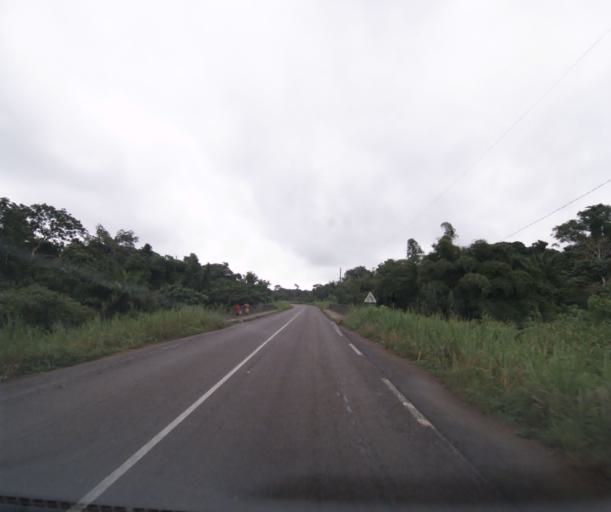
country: CM
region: Littoral
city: Dizangue
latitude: 3.5005
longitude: 10.1181
